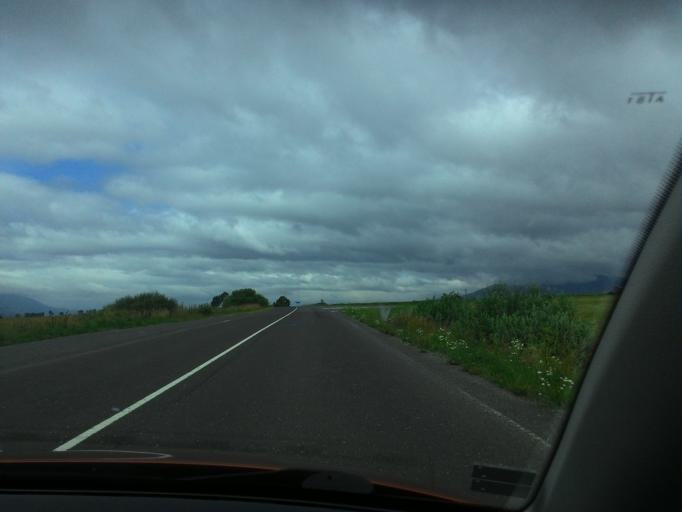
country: SK
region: Zilinsky
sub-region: Okres Liptovsky Mikulas
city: Hybe
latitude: 49.0653
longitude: 19.9145
